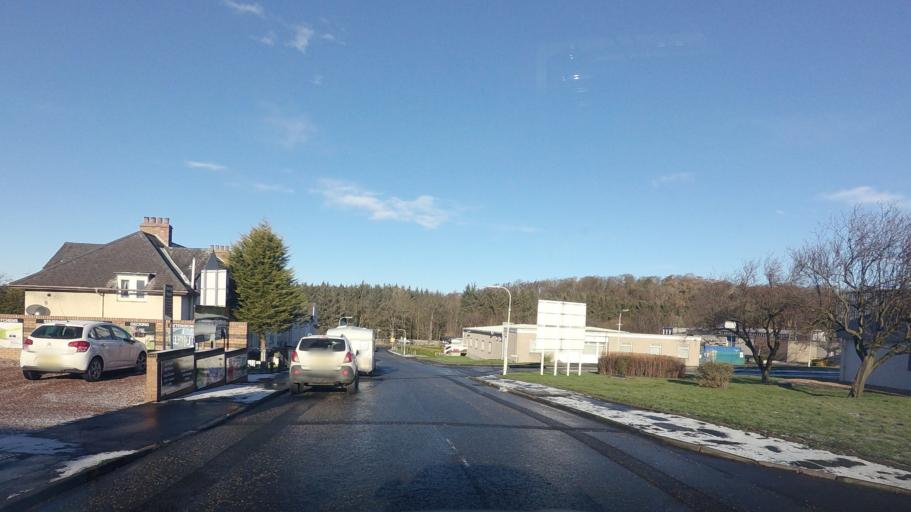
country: GB
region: Scotland
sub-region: Fife
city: Crossgates
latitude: 56.0446
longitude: -3.3479
